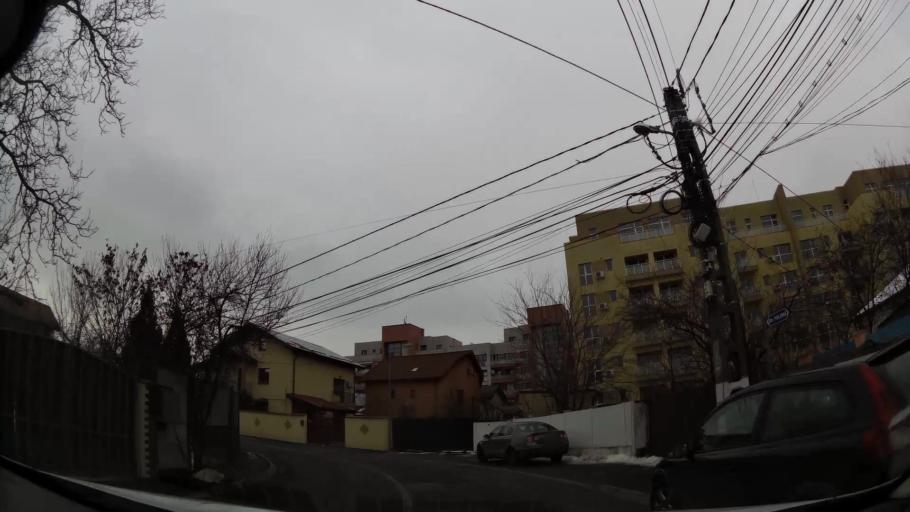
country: RO
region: Ilfov
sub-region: Comuna Otopeni
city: Otopeni
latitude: 44.5468
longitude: 26.0763
